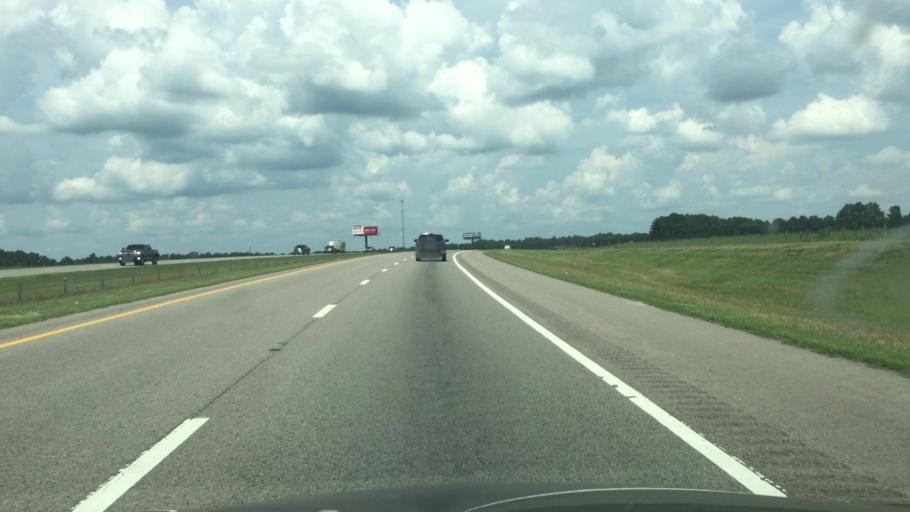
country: US
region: North Carolina
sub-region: Richmond County
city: Ellerbe
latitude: 35.1890
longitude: -79.7239
